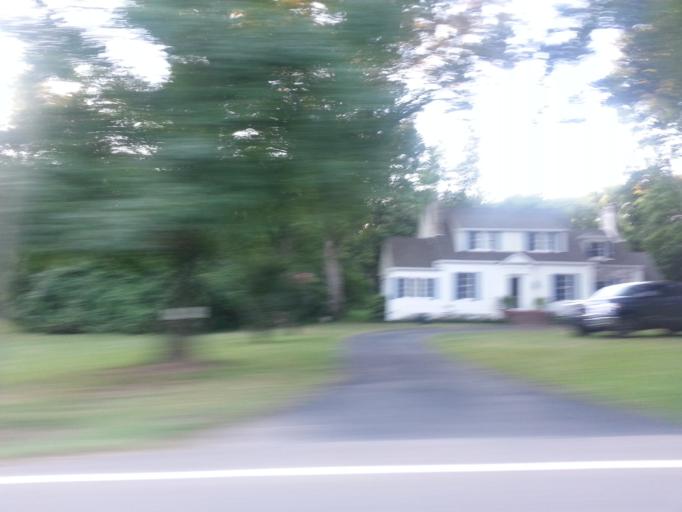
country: US
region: Tennessee
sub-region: Knox County
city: Knoxville
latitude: 35.9723
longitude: -83.8791
